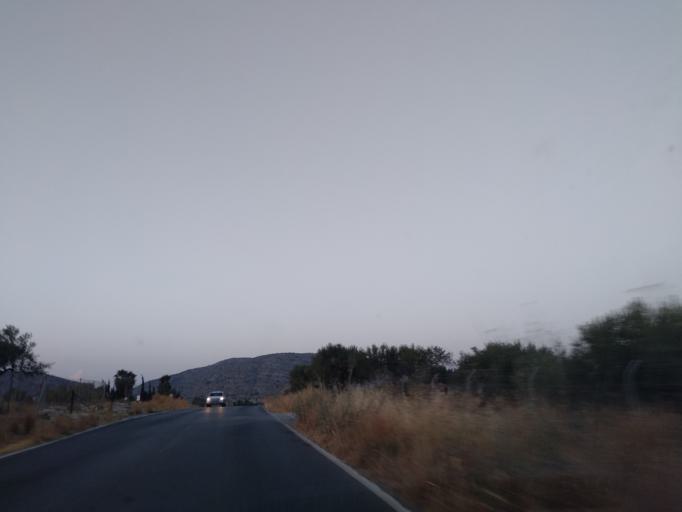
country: ES
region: Andalusia
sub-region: Provincia de Malaga
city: Cartama
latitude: 36.6791
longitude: -4.6579
